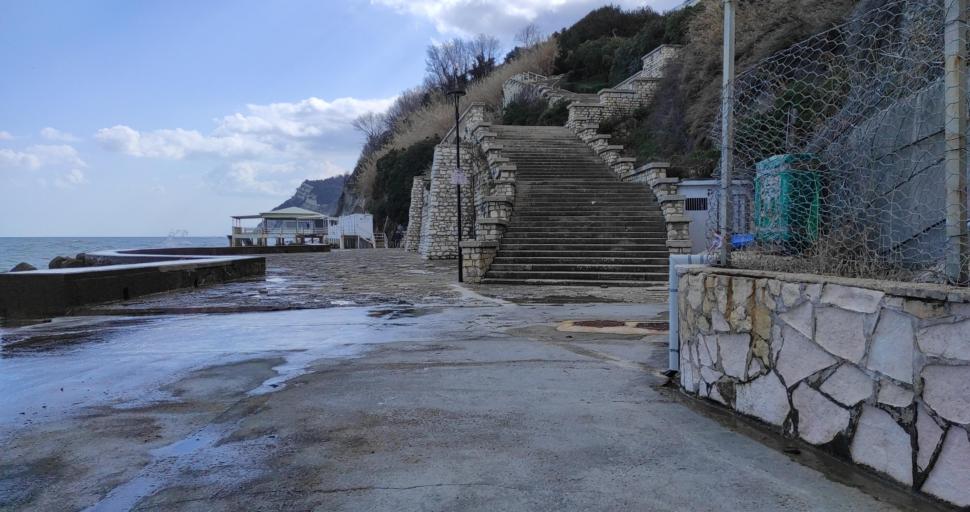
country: IT
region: The Marches
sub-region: Provincia di Ancona
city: Pietra la Croce
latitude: 43.6158
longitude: 13.5343
